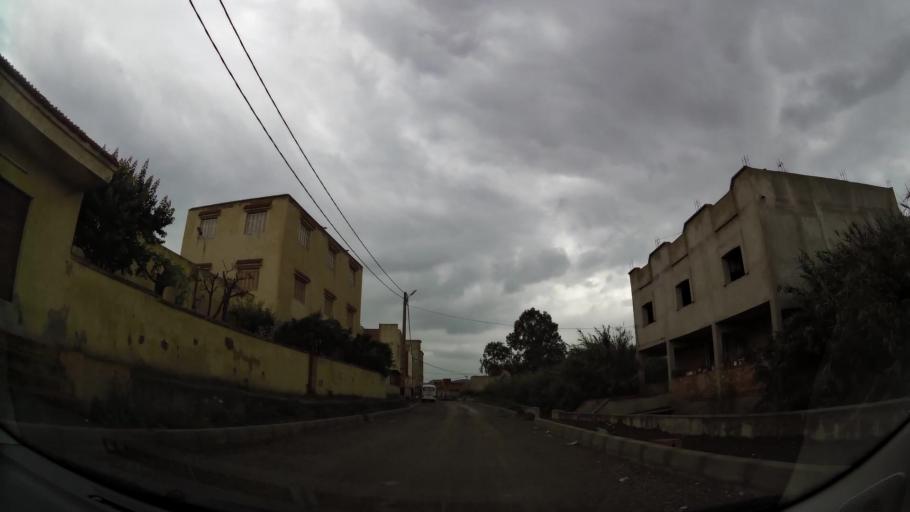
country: MA
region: Oriental
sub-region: Nador
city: Nador
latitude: 35.1486
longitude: -2.9841
